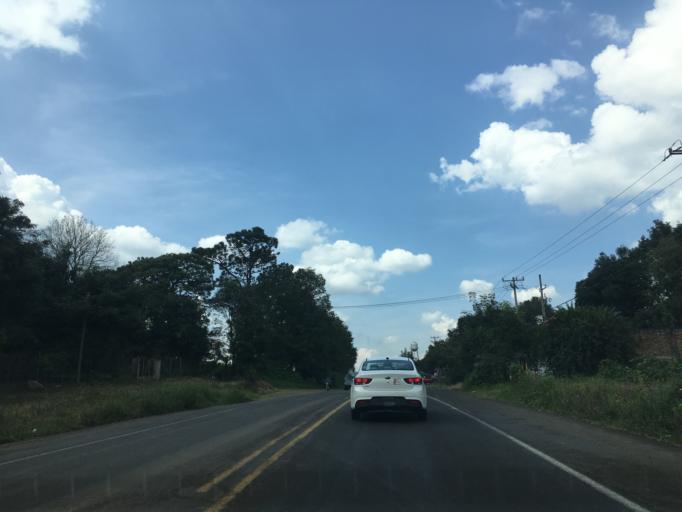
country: MX
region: Michoacan
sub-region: Tingueindin
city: Tingueindin
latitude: 19.7567
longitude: -102.4902
